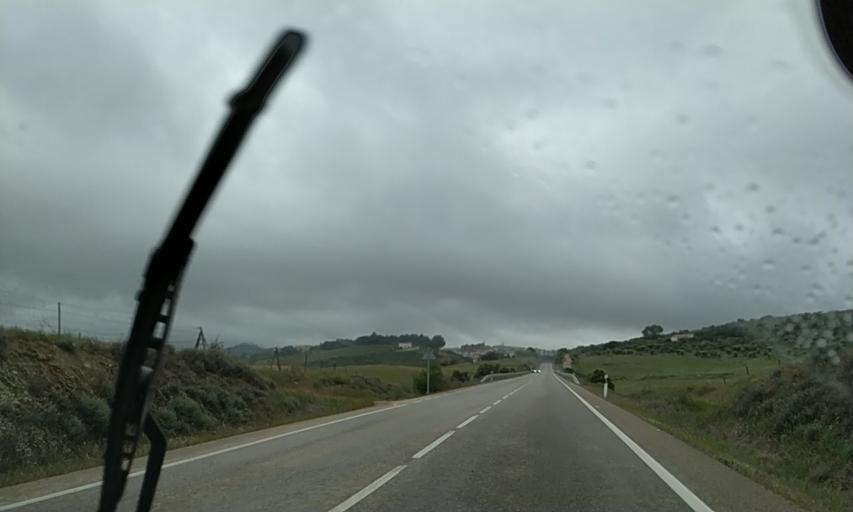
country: ES
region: Extremadura
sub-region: Provincia de Caceres
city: Caceres
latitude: 39.4934
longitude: -6.3852
